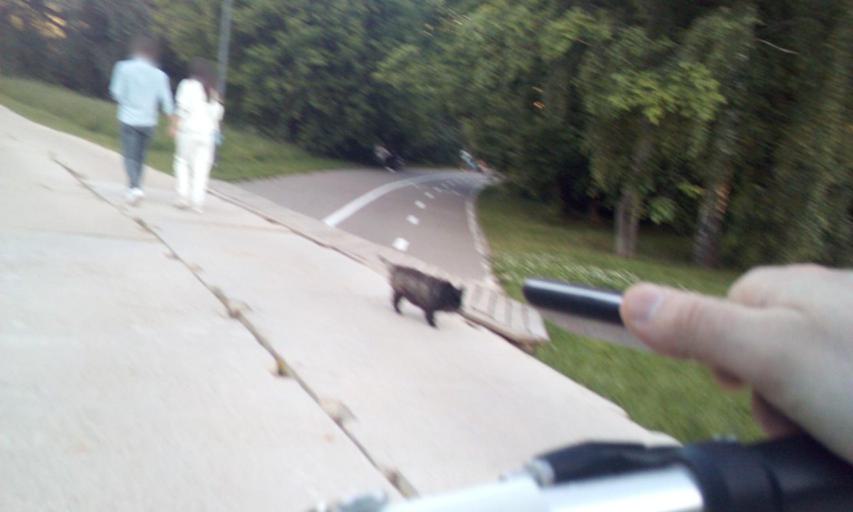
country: RU
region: Moscow
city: Ramenki
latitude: 55.6822
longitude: 37.5074
